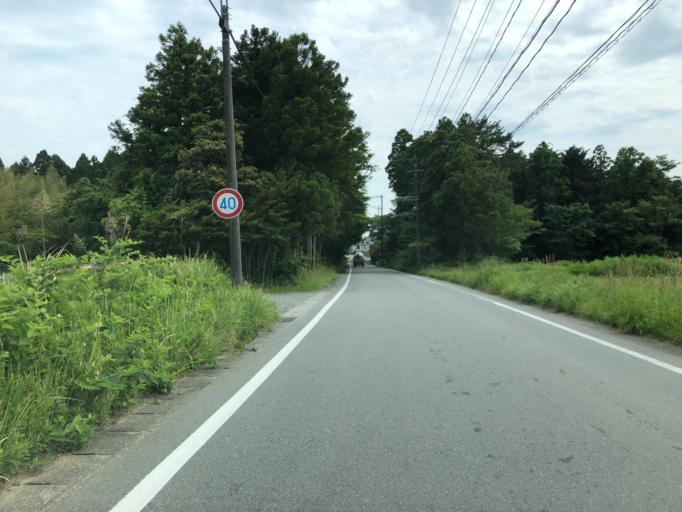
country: JP
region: Fukushima
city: Namie
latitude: 37.3021
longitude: 140.9998
